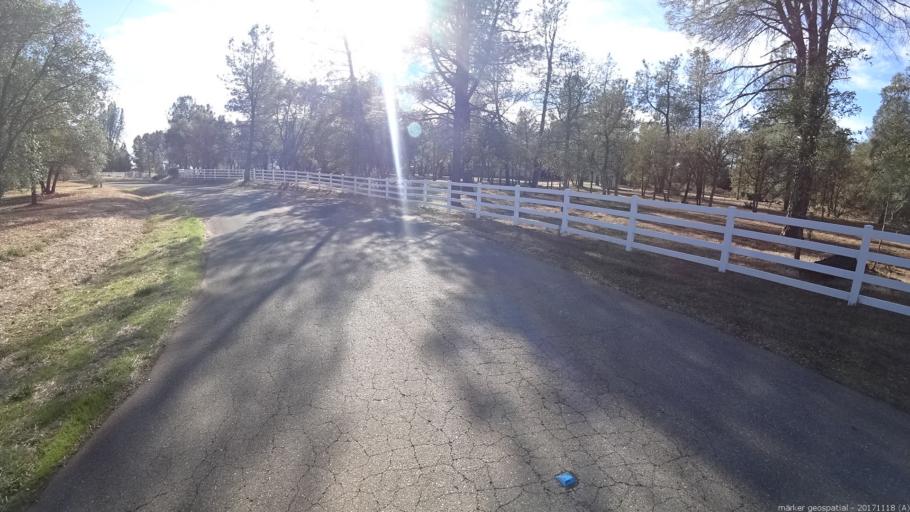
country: US
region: California
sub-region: Shasta County
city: Redding
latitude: 40.4808
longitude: -122.4437
